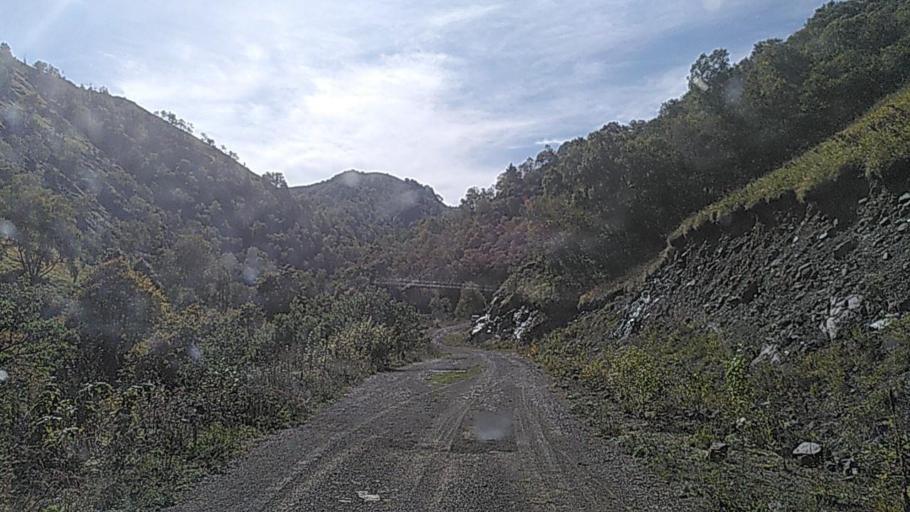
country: RU
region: Kabardino-Balkariya
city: Kamennomostskoye
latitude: 43.7170
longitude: 42.8451
